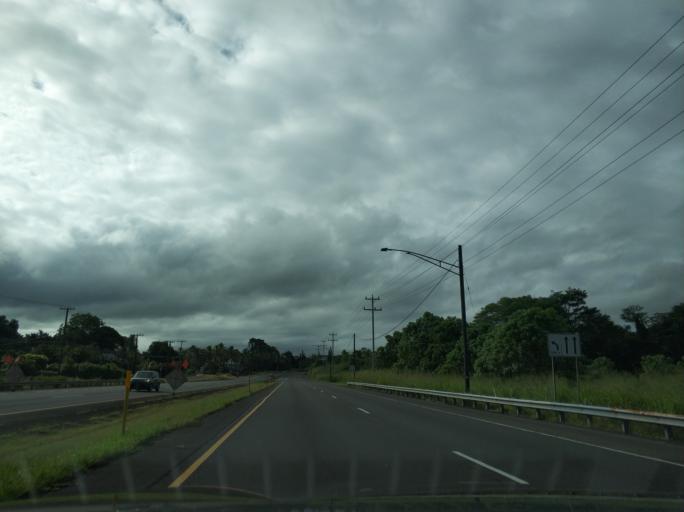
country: US
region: Hawaii
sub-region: Hawaii County
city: Kea'au
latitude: 19.6296
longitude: -155.0398
